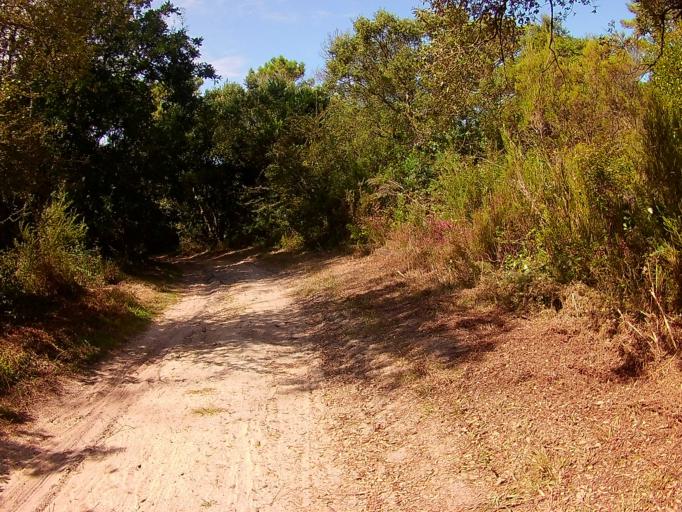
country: FR
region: Aquitaine
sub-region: Departement des Landes
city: Labenne
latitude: 43.6066
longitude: -1.4608
